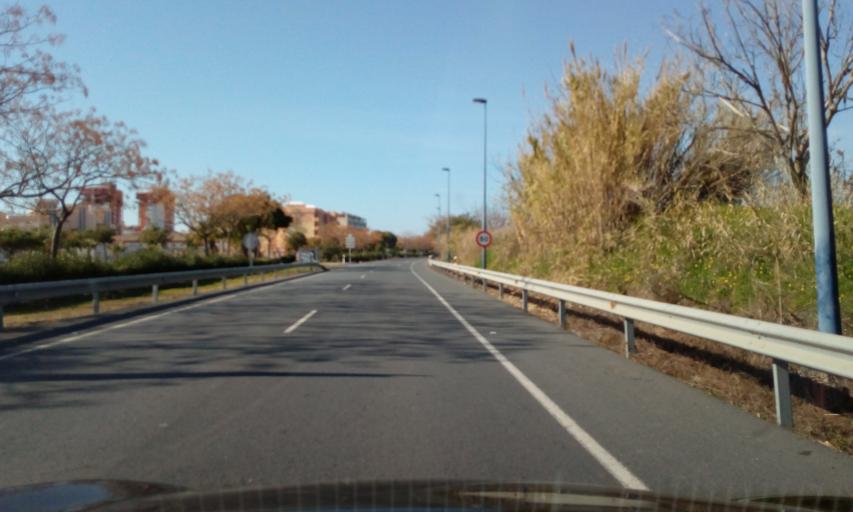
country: ES
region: Andalusia
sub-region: Provincia de Huelva
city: Lepe
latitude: 37.2107
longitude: -7.2024
